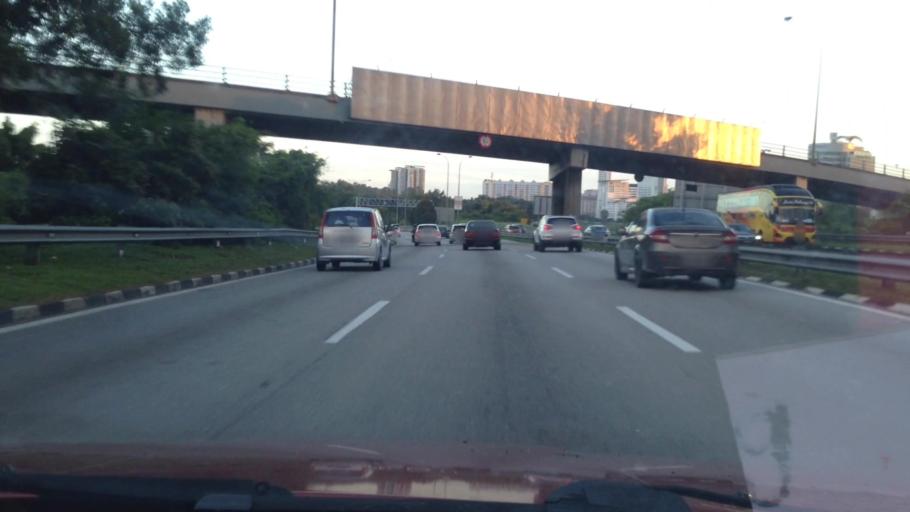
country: MY
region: Selangor
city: Shah Alam
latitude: 3.0924
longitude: 101.5502
